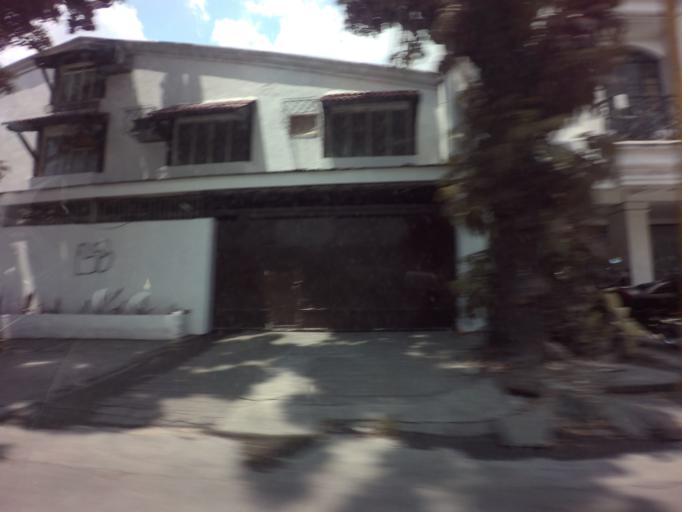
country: PH
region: Metro Manila
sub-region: Mandaluyong
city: Mandaluyong City
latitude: 14.5723
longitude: 121.0263
